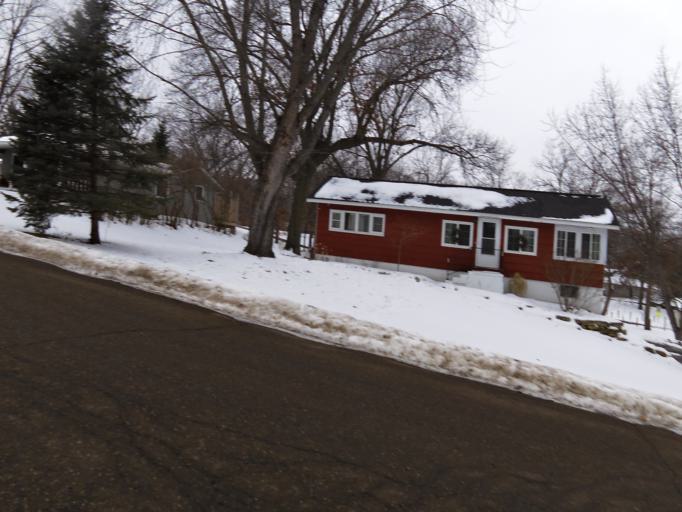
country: US
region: Wisconsin
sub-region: Saint Croix County
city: Hudson
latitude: 44.9737
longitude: -92.7508
